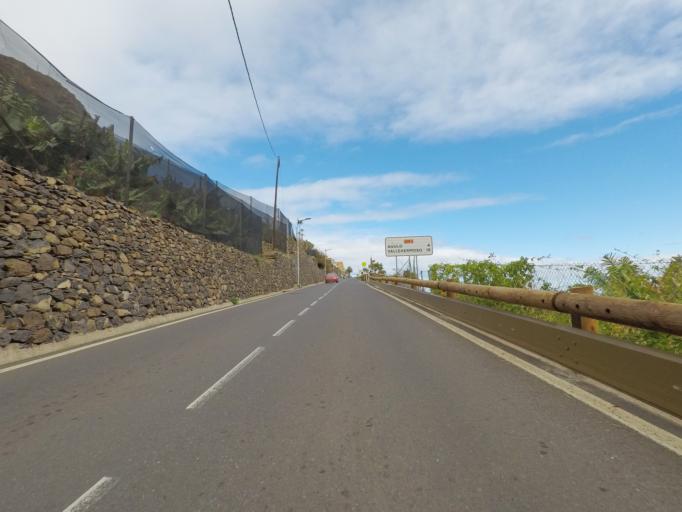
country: ES
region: Canary Islands
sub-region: Provincia de Santa Cruz de Tenerife
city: Hermigua
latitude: 28.1763
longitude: -17.1862
